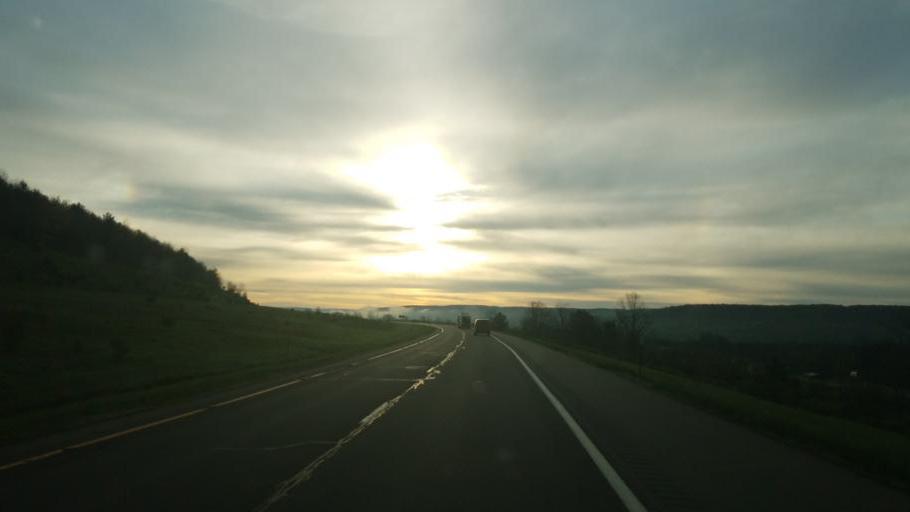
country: US
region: New York
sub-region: Allegany County
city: Friendship
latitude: 42.2021
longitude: -78.1635
